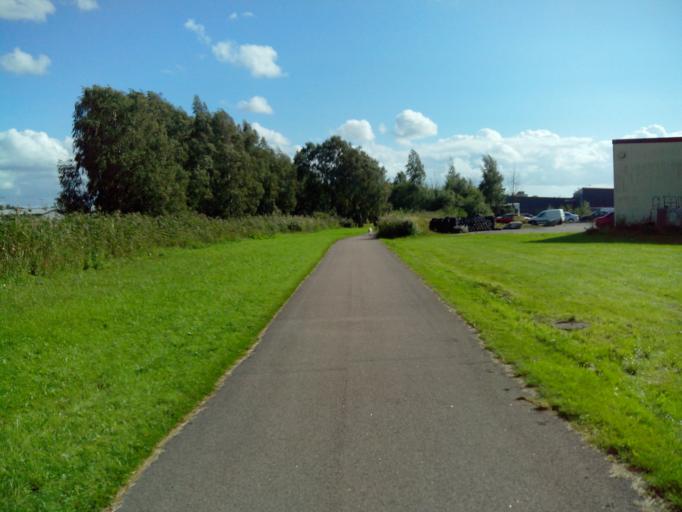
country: SE
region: Vaestra Goetaland
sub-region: Goteborg
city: Goeteborg
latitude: 57.7344
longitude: 11.9521
